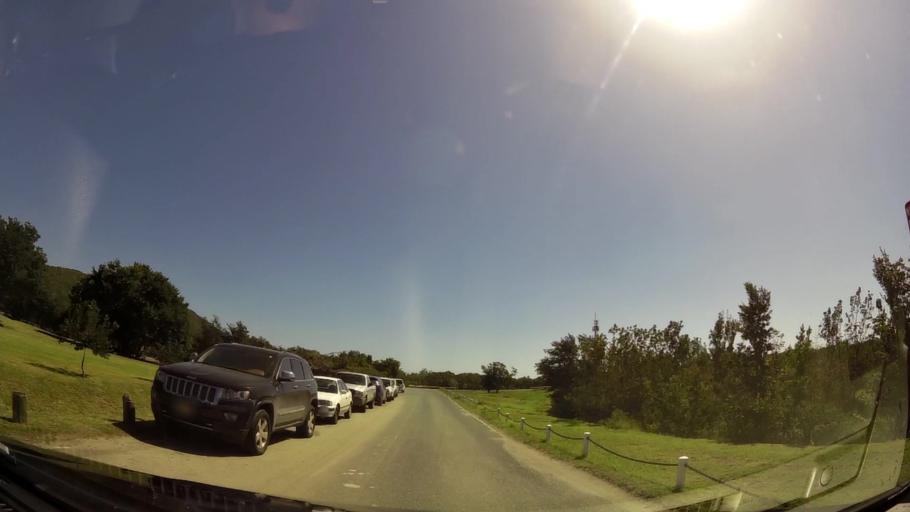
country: VG
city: Tortola
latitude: 18.4448
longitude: -64.5355
